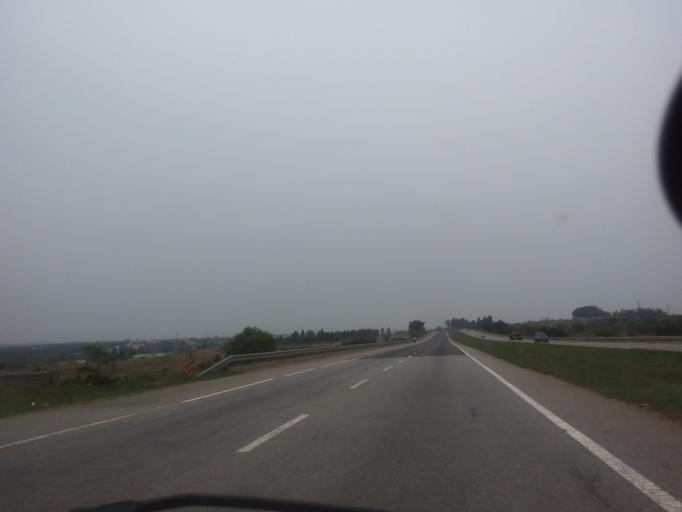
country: IN
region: Karnataka
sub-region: Bangalore Urban
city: Bangalore
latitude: 12.9159
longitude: 77.4678
